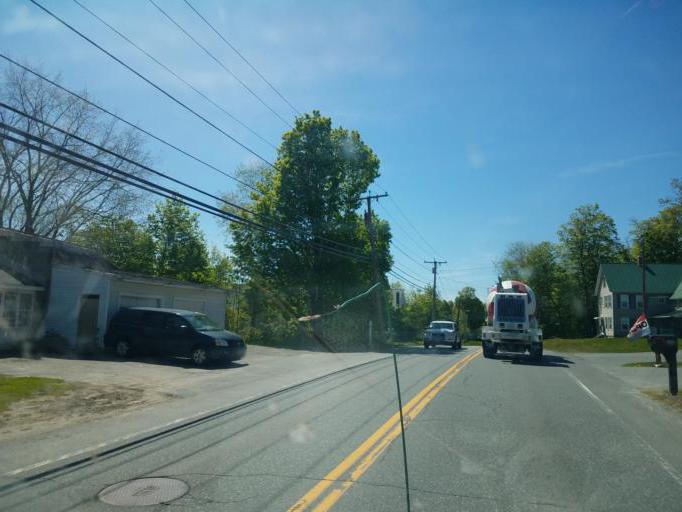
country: US
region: New Hampshire
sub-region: Grafton County
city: Enfield
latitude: 43.6431
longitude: -72.1308
